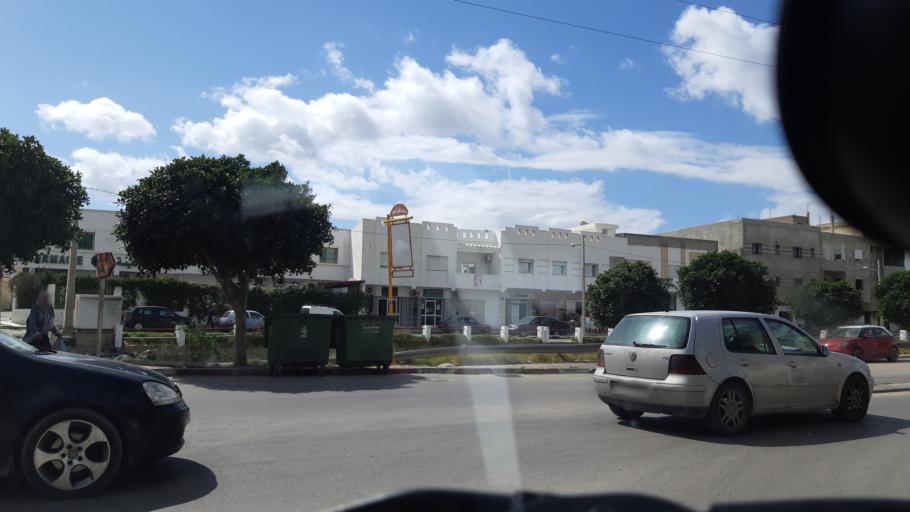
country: TN
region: Susah
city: Akouda
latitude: 35.8767
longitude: 10.5364
